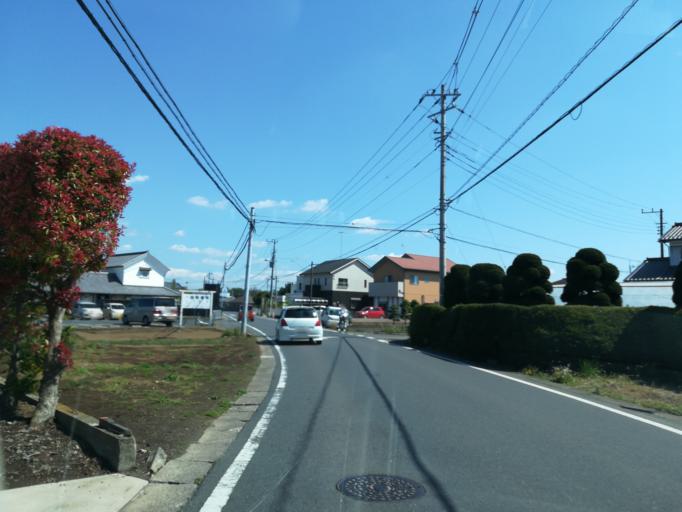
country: JP
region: Ibaraki
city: Naka
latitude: 36.0745
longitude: 140.1085
